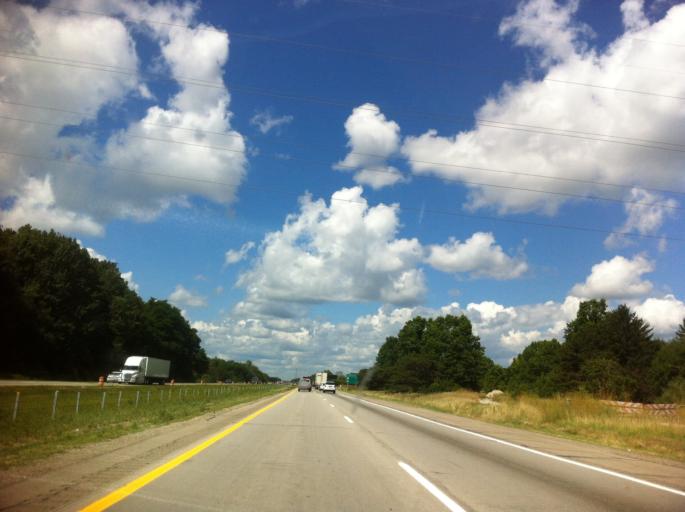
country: US
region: Michigan
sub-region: Washtenaw County
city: Milan
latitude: 42.1785
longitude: -83.6845
